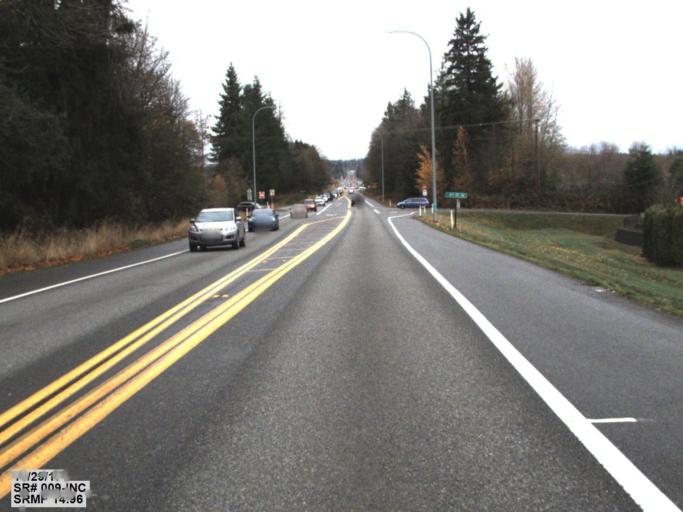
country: US
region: Washington
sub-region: Snohomish County
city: West Lake Stevens
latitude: 47.9913
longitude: -122.1044
